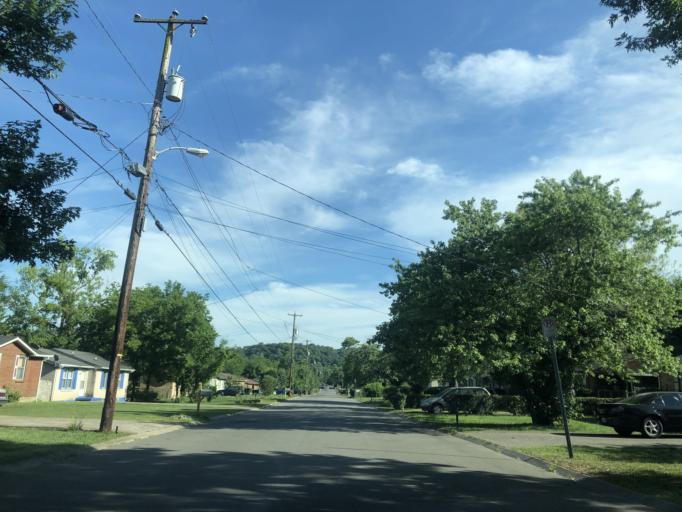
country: US
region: Tennessee
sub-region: Davidson County
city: Nashville
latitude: 36.2149
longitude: -86.8340
